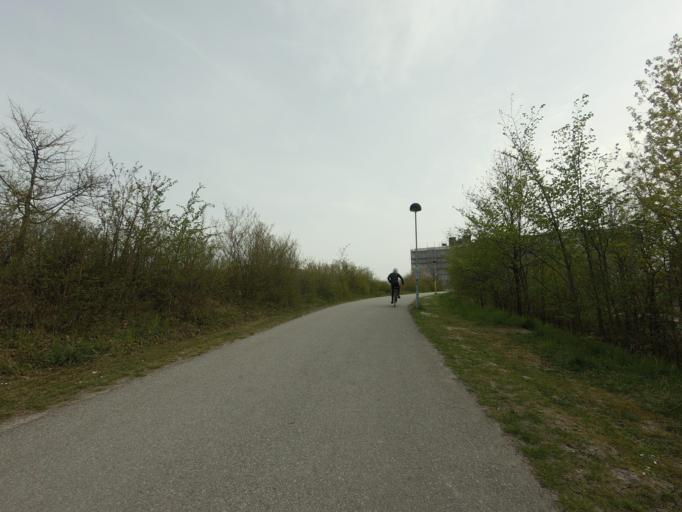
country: SE
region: Skane
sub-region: Lunds Kommun
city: Lund
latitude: 55.7124
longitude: 13.1847
